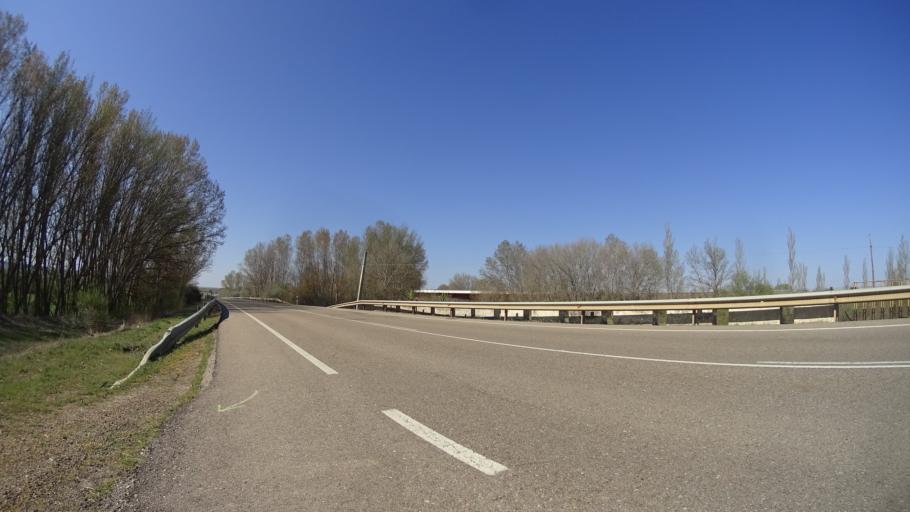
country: ES
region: Castille and Leon
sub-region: Provincia de Palencia
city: Fromista
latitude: 42.2508
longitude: -4.4163
